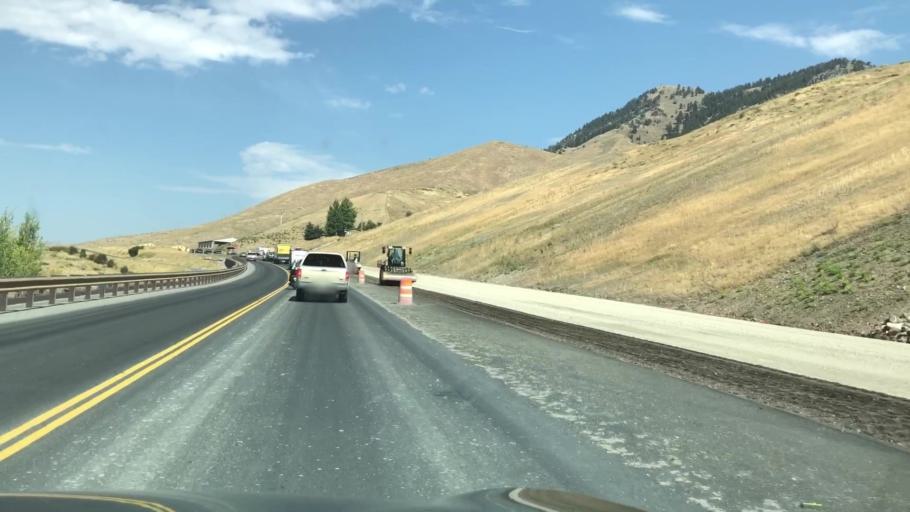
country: US
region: Wyoming
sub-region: Teton County
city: South Park
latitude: 43.3966
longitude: -110.7494
